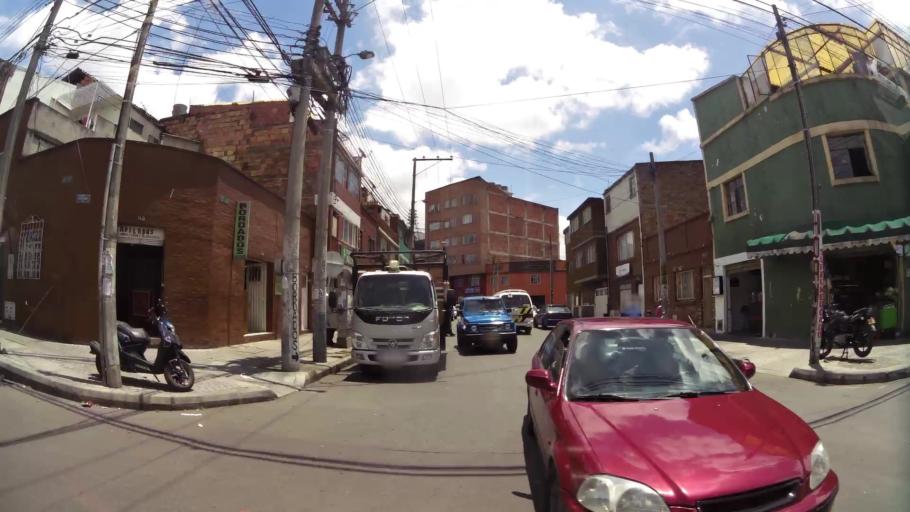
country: CO
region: Bogota D.C.
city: Bogota
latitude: 4.5894
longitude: -74.1065
